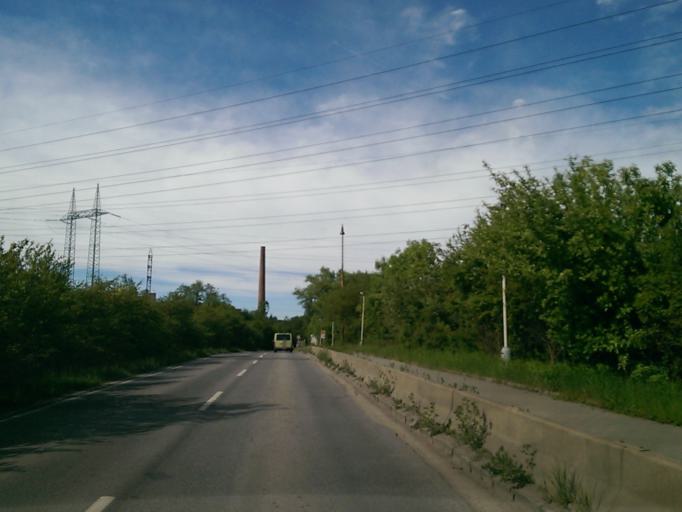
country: CZ
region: Praha
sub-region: Praha 20
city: Horni Pocernice
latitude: 50.0849
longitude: 14.6168
